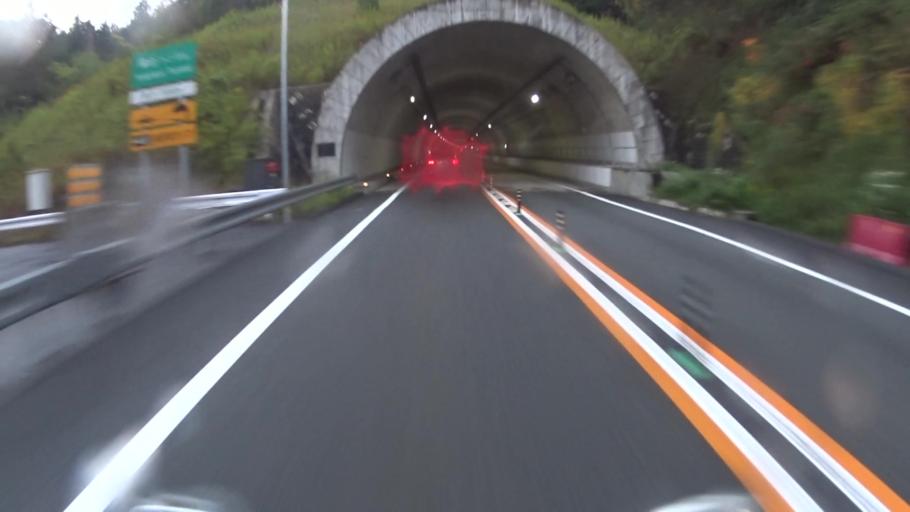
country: JP
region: Kyoto
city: Ayabe
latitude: 35.3322
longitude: 135.3114
